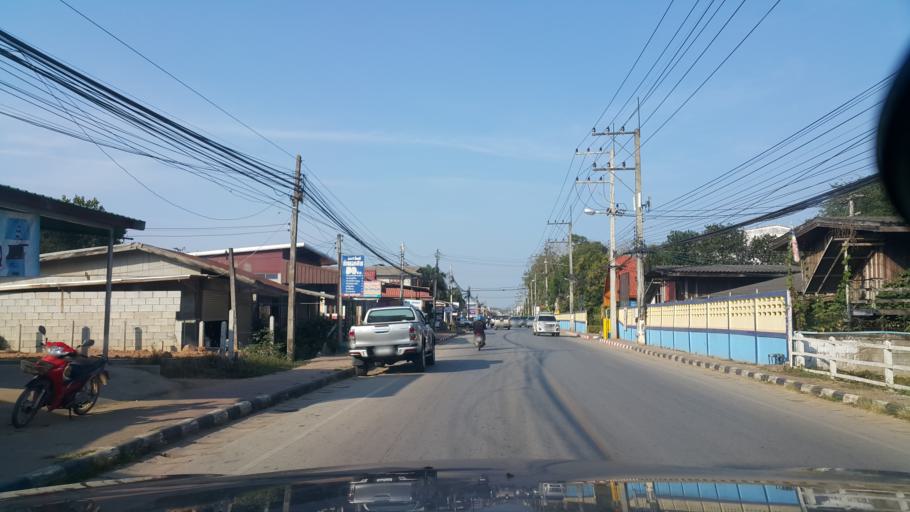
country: TH
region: Loei
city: Chiang Khan
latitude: 17.8951
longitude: 101.6588
